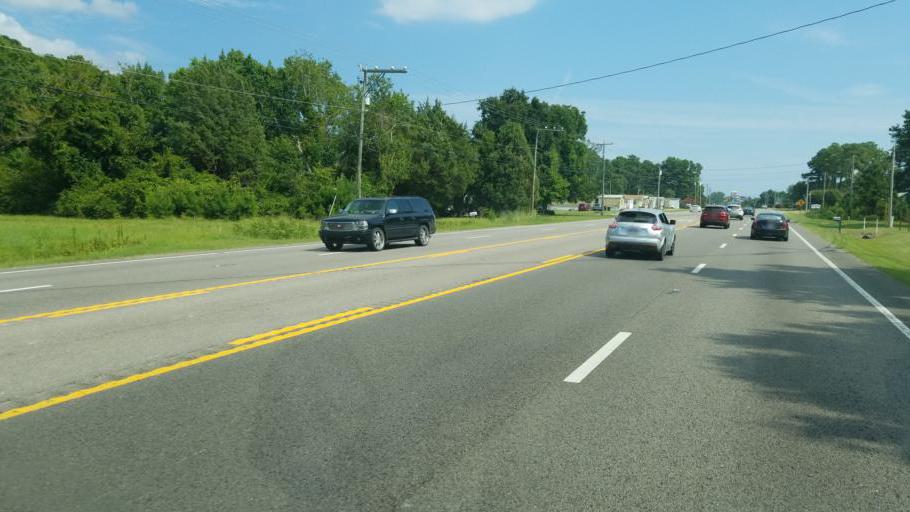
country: US
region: North Carolina
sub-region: Dare County
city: Southern Shores
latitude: 36.1242
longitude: -75.8352
